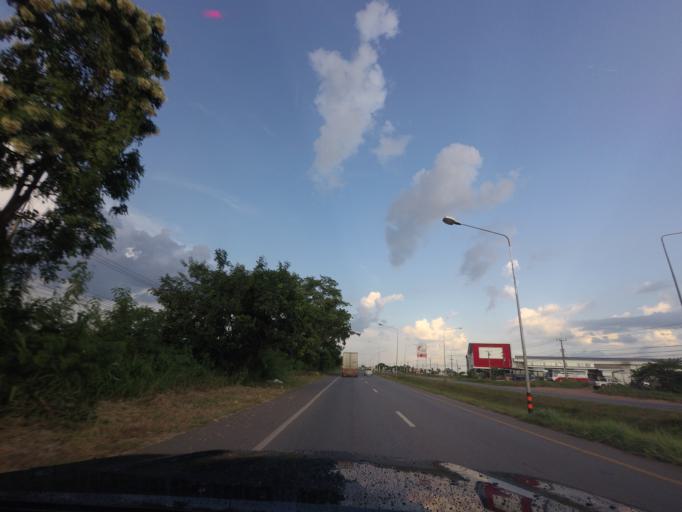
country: TH
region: Khon Kaen
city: Khon Kaen
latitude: 16.3891
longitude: 102.8375
